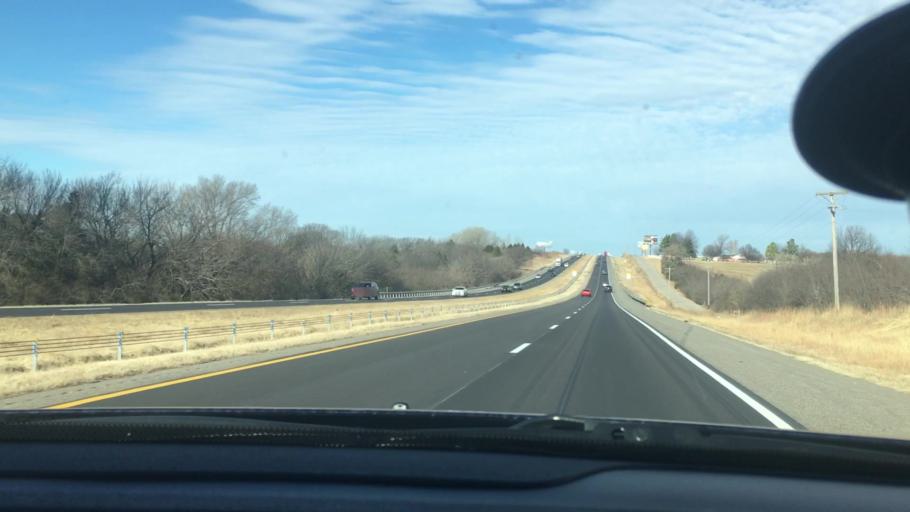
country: US
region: Oklahoma
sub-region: Cleveland County
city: Noble
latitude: 35.0859
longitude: -97.4142
